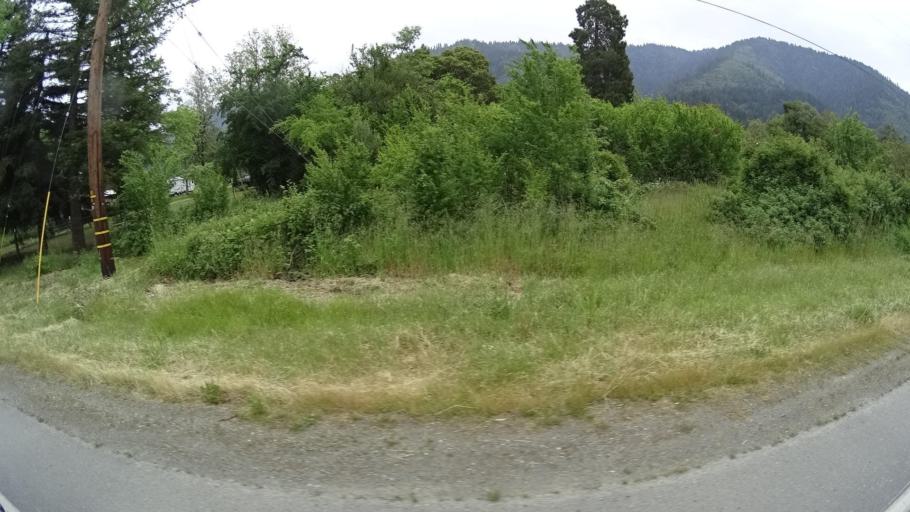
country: US
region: California
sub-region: Humboldt County
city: Willow Creek
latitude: 41.0564
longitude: -123.6815
